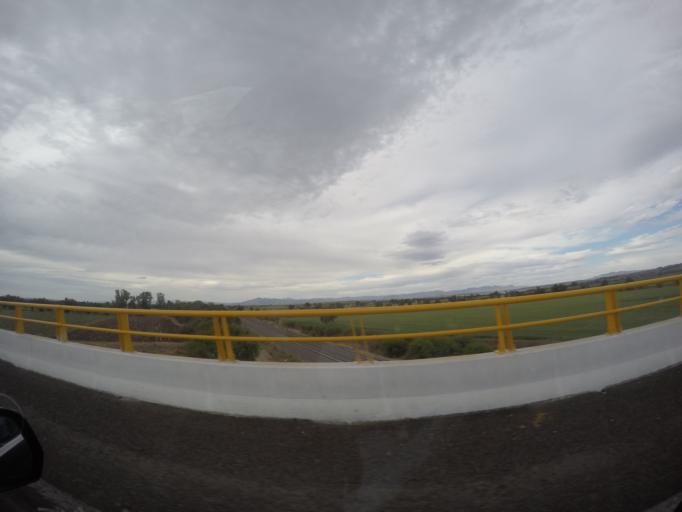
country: MX
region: Guanajuato
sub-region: Irapuato
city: Serrano
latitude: 20.7837
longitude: -101.4143
